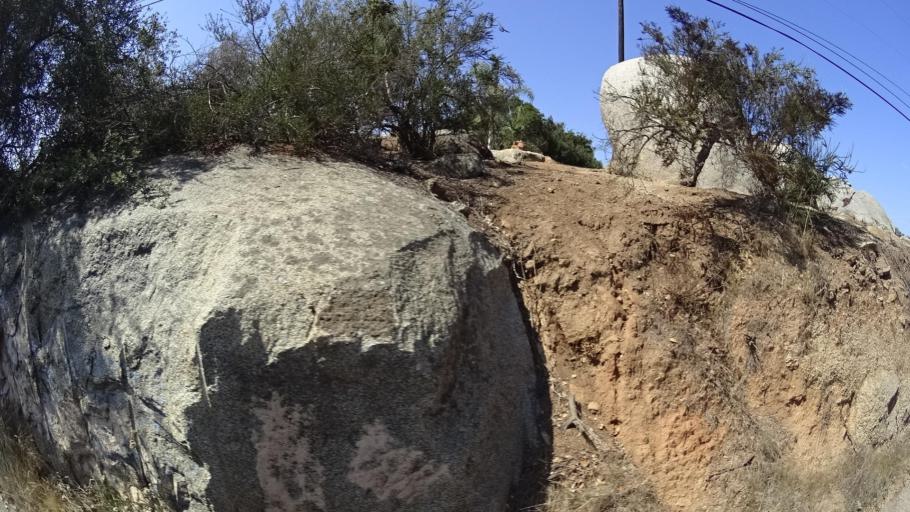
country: US
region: California
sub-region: San Diego County
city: Valley Center
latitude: 33.2333
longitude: -117.0325
